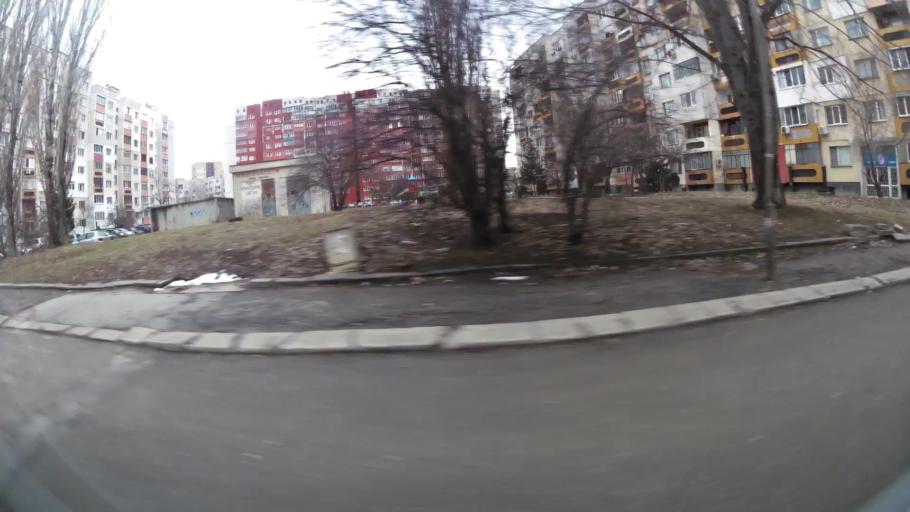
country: BG
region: Sofia-Capital
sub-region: Stolichna Obshtina
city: Sofia
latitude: 42.7299
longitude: 23.2973
